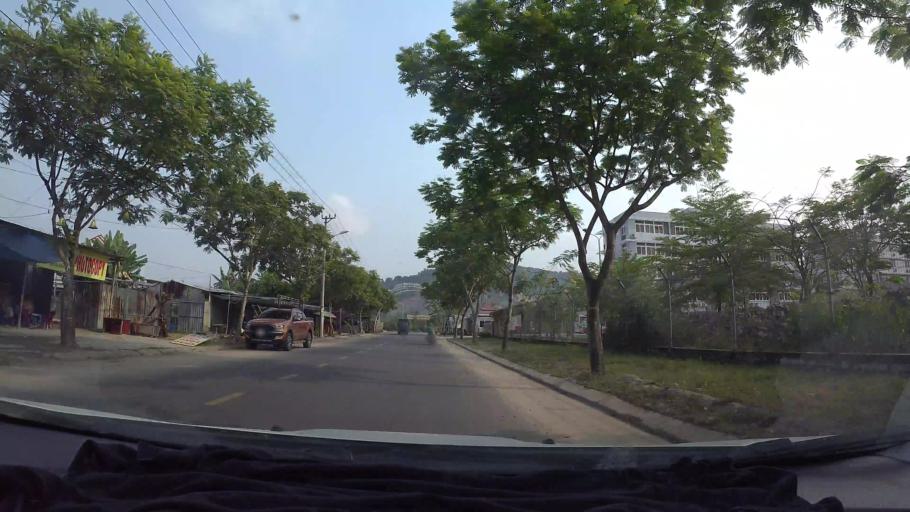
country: VN
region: Da Nang
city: Lien Chieu
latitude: 16.0498
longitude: 108.1604
